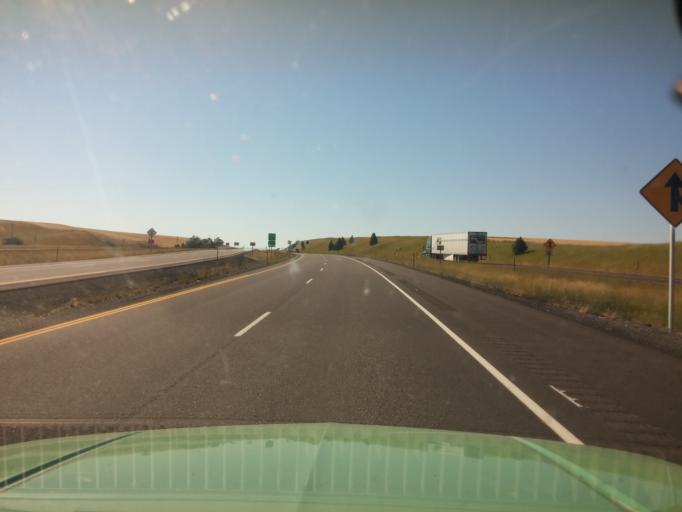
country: US
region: Washington
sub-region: Asotin County
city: Clarkston
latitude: 46.4722
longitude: -117.0354
